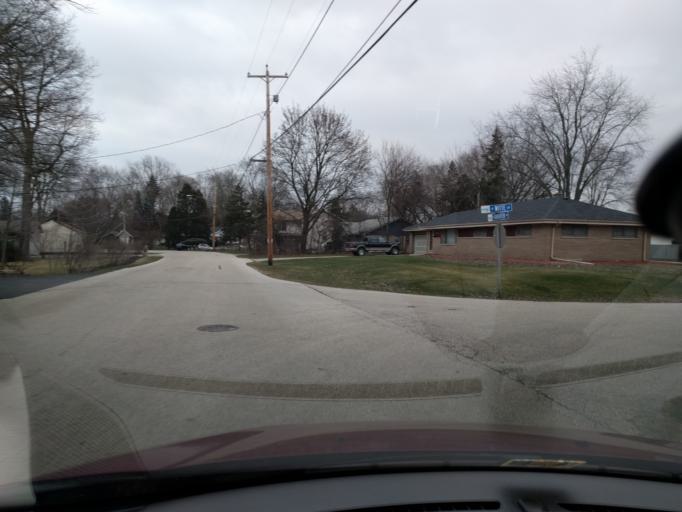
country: US
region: Wisconsin
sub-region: Milwaukee County
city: Glendale
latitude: 43.1246
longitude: -87.9247
